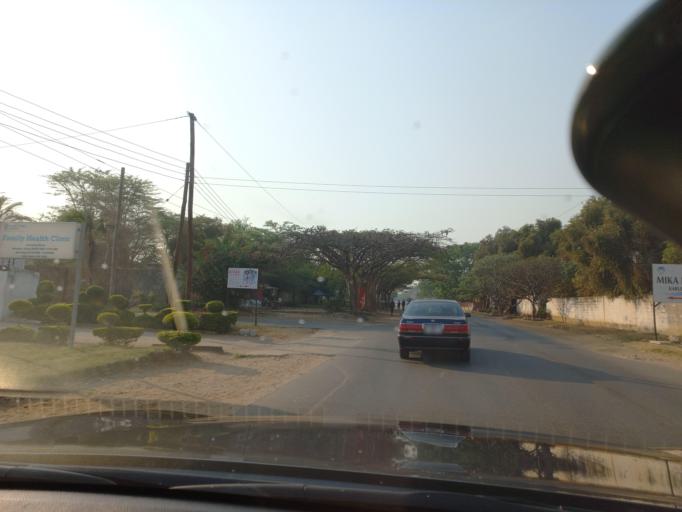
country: ZM
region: Lusaka
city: Lusaka
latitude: -15.4115
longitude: 28.3519
